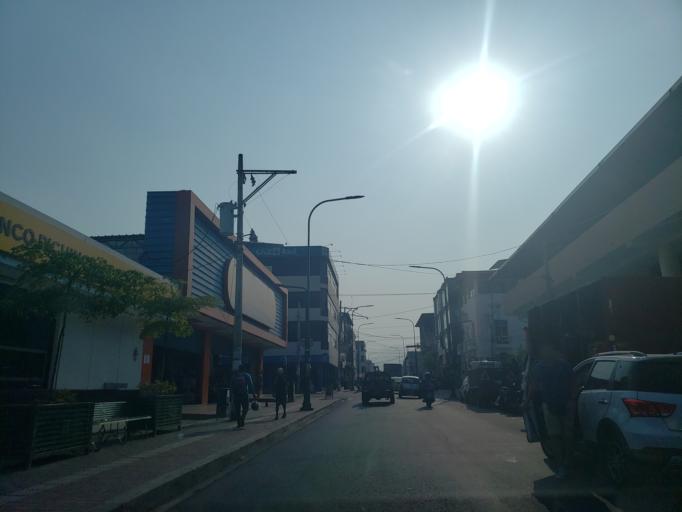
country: EC
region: Manabi
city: Manta
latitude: -0.9483
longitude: -80.7268
